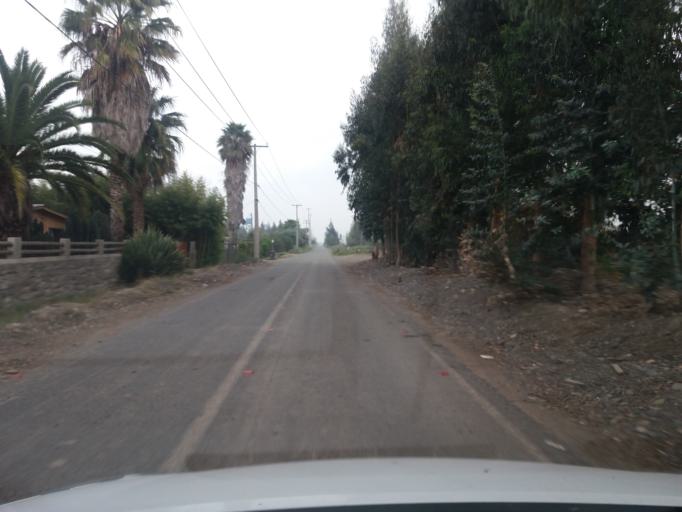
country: CL
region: Valparaiso
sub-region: Provincia de San Felipe
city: Llaillay
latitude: -32.8399
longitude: -71.0611
